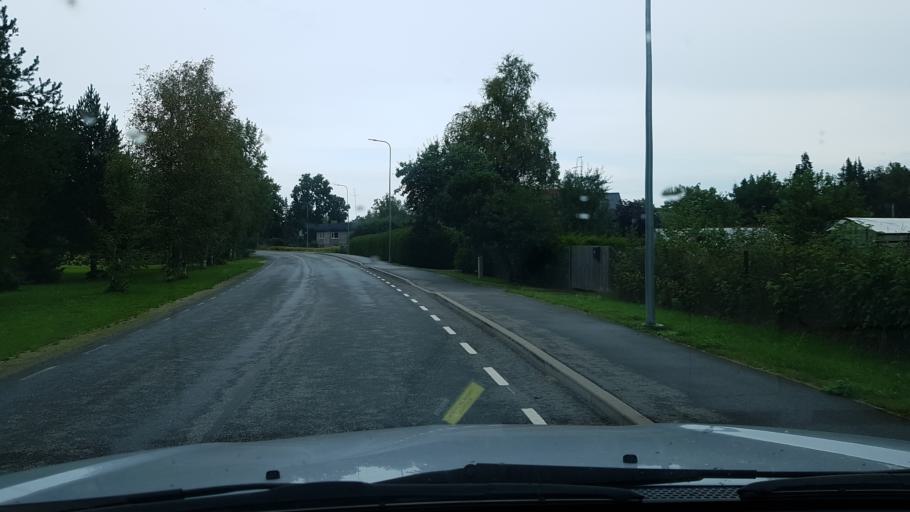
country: EE
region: Harju
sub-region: Joelaehtme vald
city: Loo
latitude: 59.3884
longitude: 24.9355
